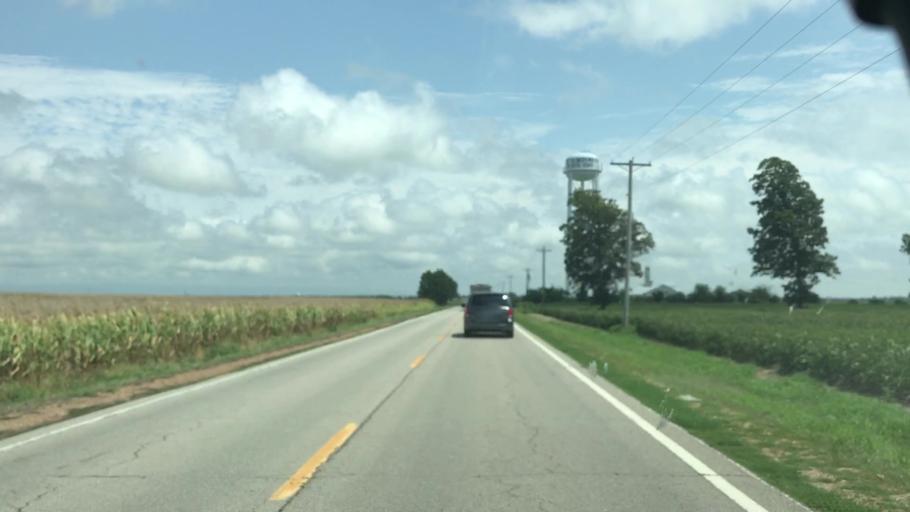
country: US
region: Missouri
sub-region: Pemiscot County
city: Hayti
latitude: 36.1760
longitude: -89.7201
